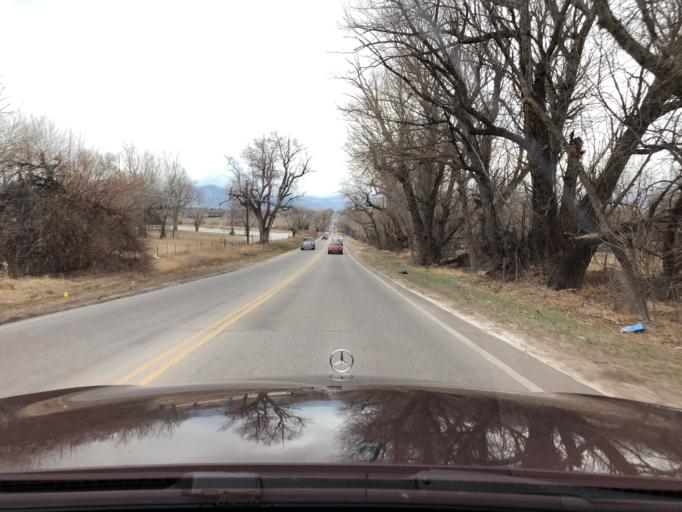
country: US
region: Colorado
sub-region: Boulder County
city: Lafayette
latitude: 40.0148
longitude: -105.1110
